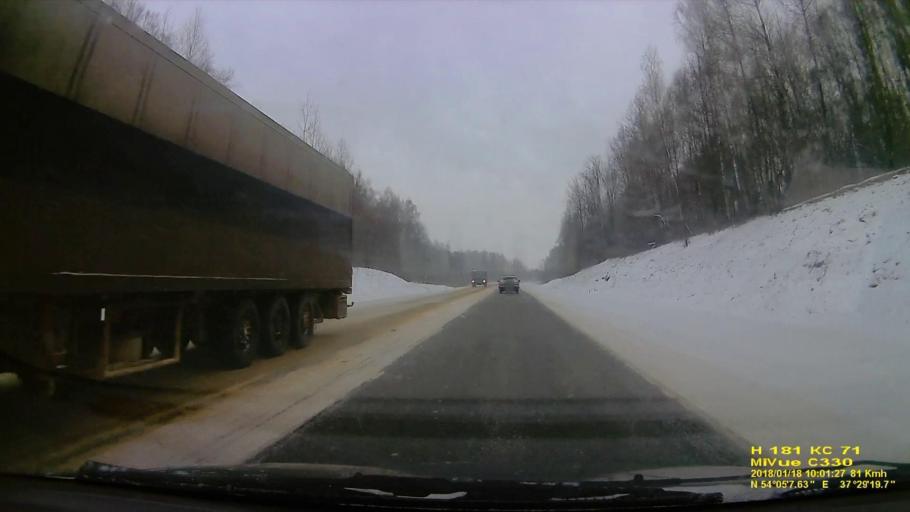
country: RU
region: Tula
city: Pervomayskiy
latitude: 54.0857
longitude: 37.4888
